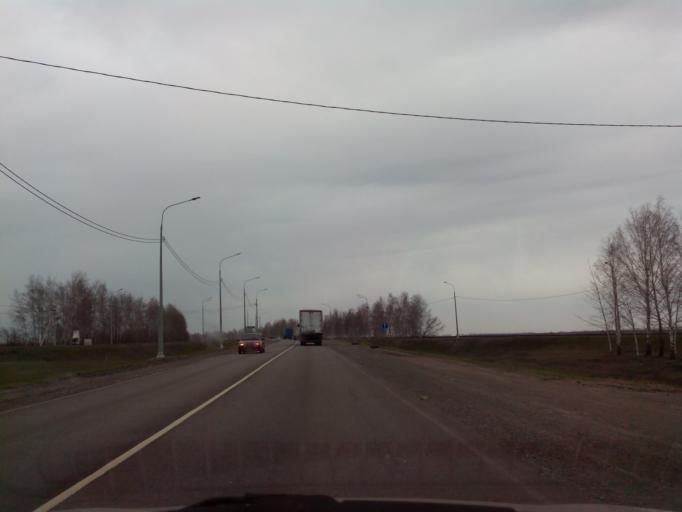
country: RU
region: Tambov
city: Pokrovo-Prigorodnoye
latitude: 52.6621
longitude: 41.3397
